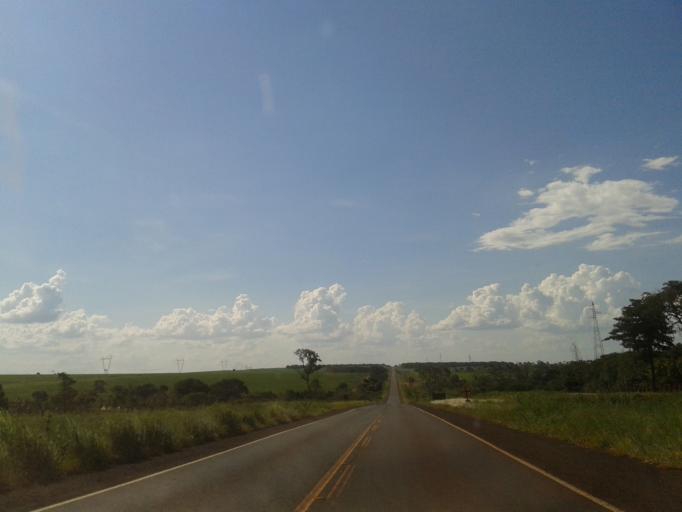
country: BR
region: Minas Gerais
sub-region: Santa Vitoria
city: Santa Vitoria
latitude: -19.0672
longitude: -50.3775
